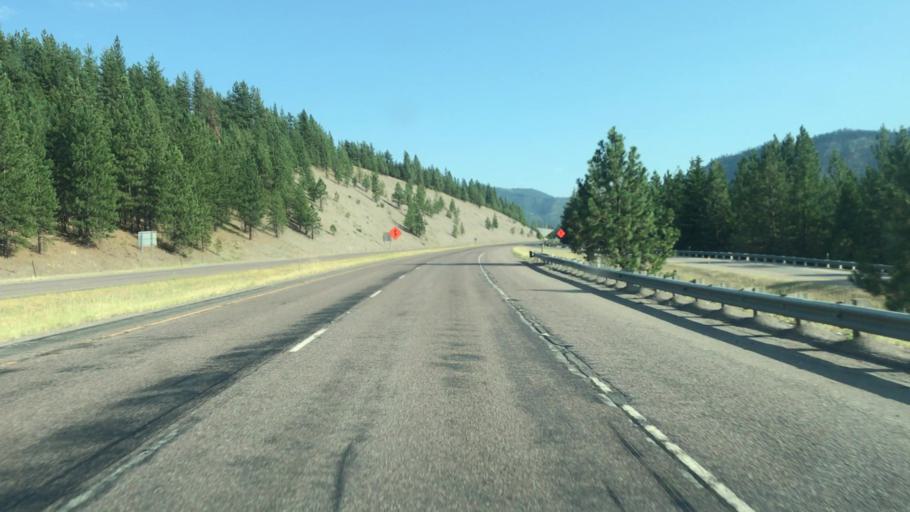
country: US
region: Montana
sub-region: Mineral County
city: Superior
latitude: 47.0245
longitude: -114.7385
